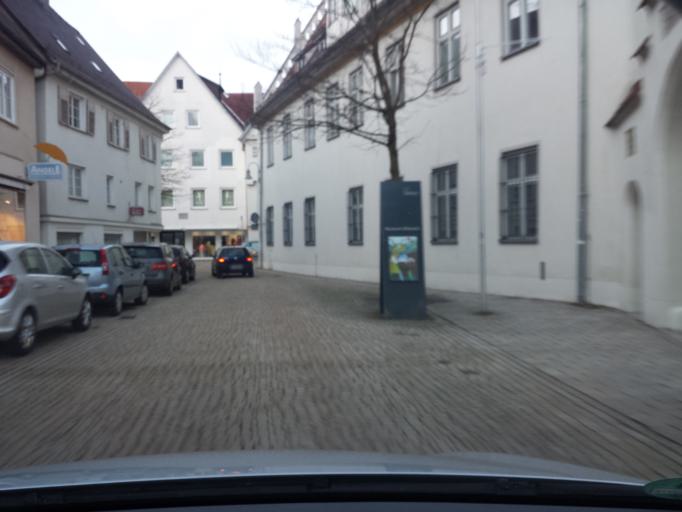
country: DE
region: Baden-Wuerttemberg
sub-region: Tuebingen Region
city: Biberach an der Riss
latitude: 48.0977
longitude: 9.7901
